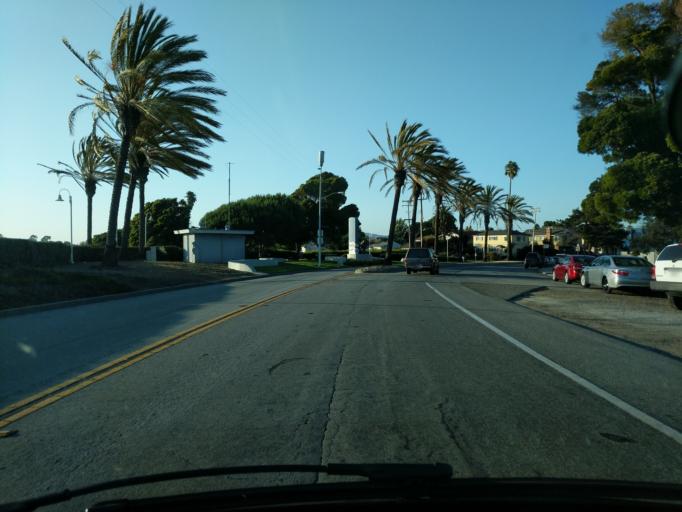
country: US
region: California
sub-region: Alameda County
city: San Leandro
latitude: 37.7003
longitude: -122.1895
